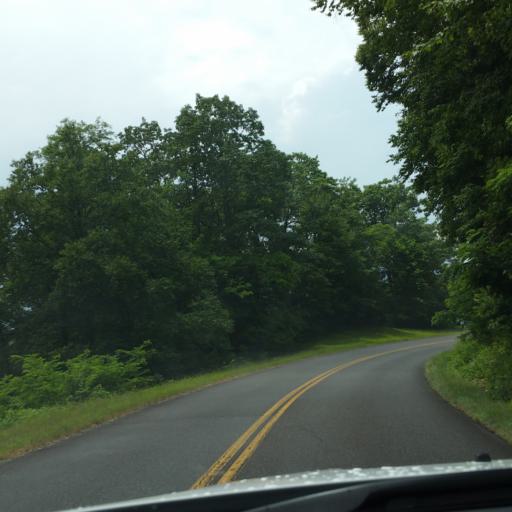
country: US
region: North Carolina
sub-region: Transylvania County
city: Brevard
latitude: 35.3397
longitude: -82.8123
